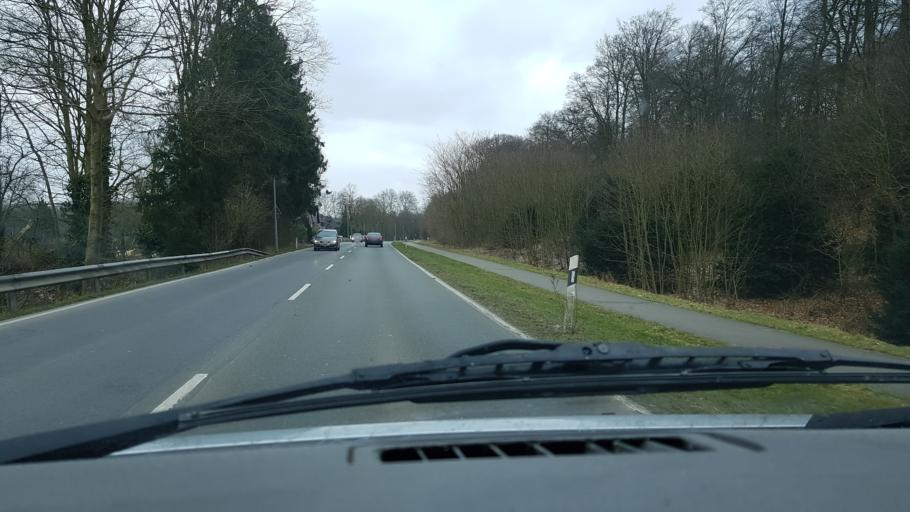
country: DE
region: North Rhine-Westphalia
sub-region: Regierungsbezirk Dusseldorf
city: Kleve
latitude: 51.7998
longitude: 6.1131
